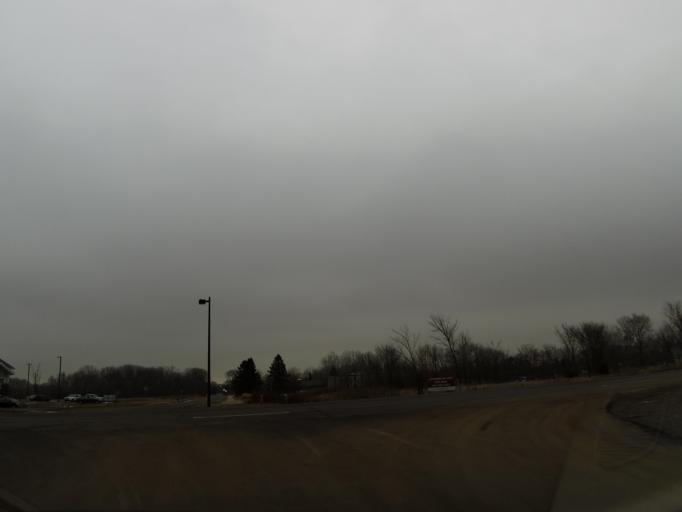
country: US
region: Minnesota
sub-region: Washington County
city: Lake Elmo
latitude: 45.0054
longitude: -92.8835
